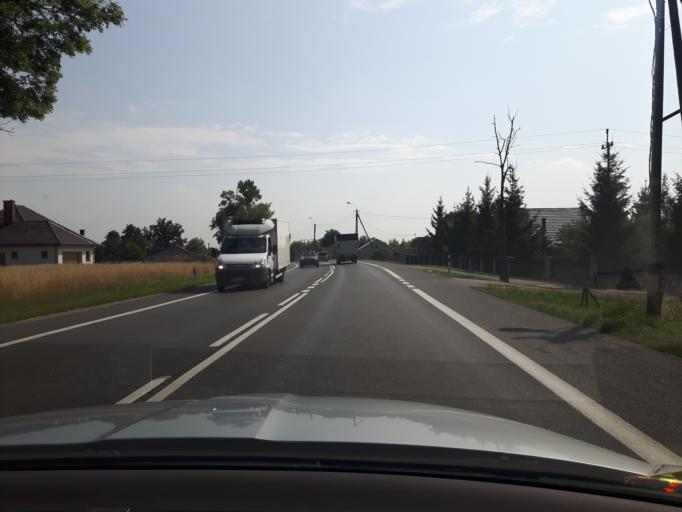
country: PL
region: Masovian Voivodeship
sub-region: Powiat mlawski
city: Wisniewo
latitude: 53.0035
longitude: 20.3291
